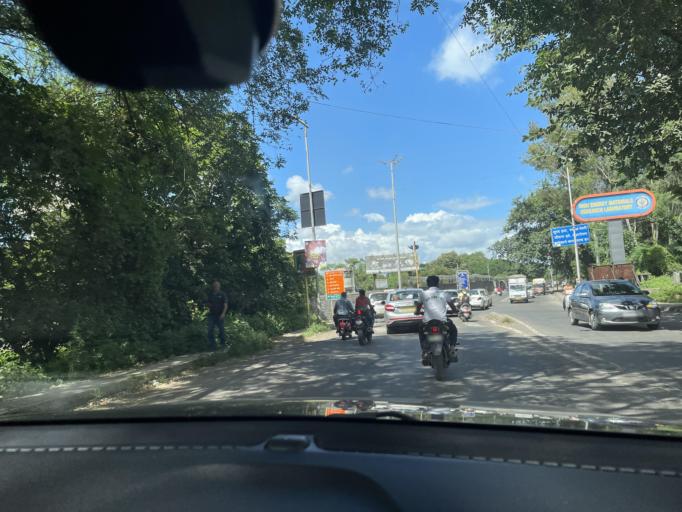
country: IN
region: Maharashtra
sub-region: Pune Division
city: Shivaji Nagar
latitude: 18.5253
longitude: 73.7812
